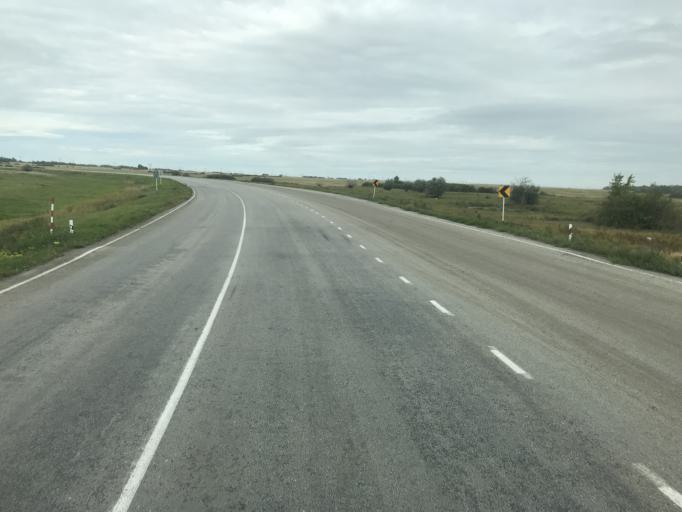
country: RU
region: Chelyabinsk
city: Bobrovka
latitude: 53.9863
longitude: 61.7033
